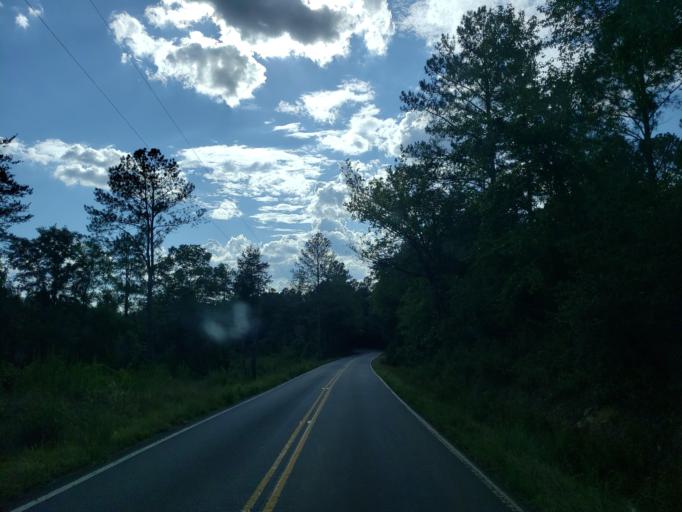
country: US
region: Georgia
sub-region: Bartow County
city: Euharlee
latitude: 34.1841
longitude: -85.0468
